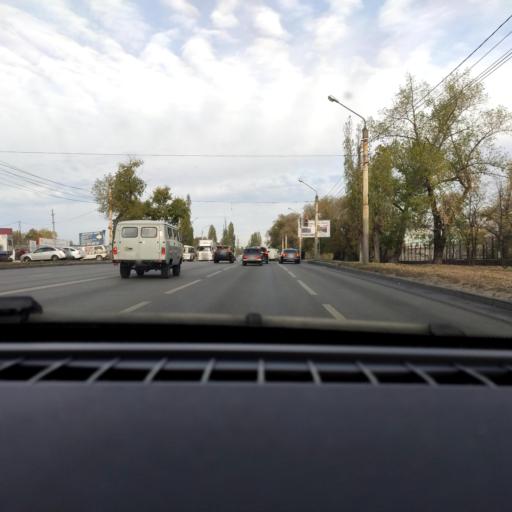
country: RU
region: Voronezj
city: Voronezh
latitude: 51.6258
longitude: 39.2320
